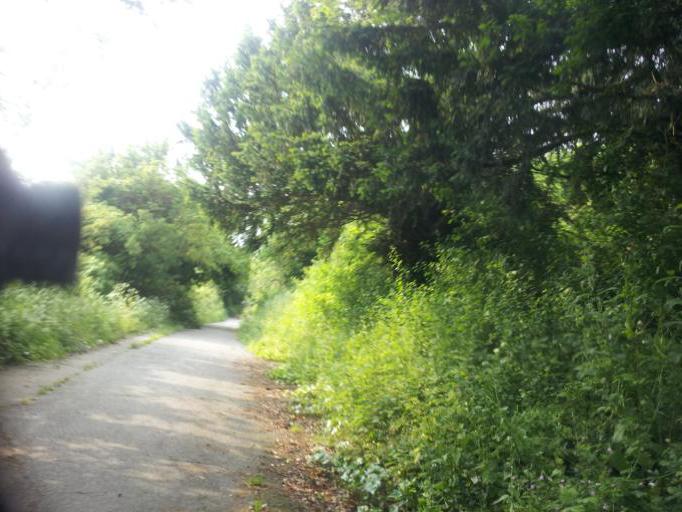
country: GB
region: England
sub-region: Kent
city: Gillingham
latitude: 51.3628
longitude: 0.5658
